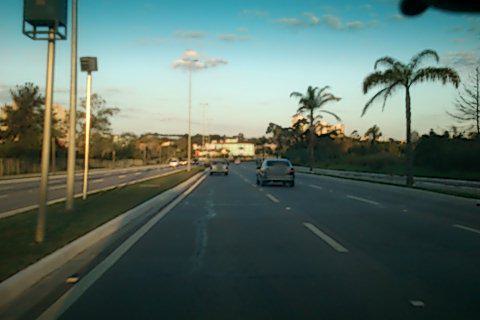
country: BR
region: Sao Paulo
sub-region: Sao Jose Dos Campos
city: Sao Jose dos Campos
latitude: -23.1657
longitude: -45.8978
